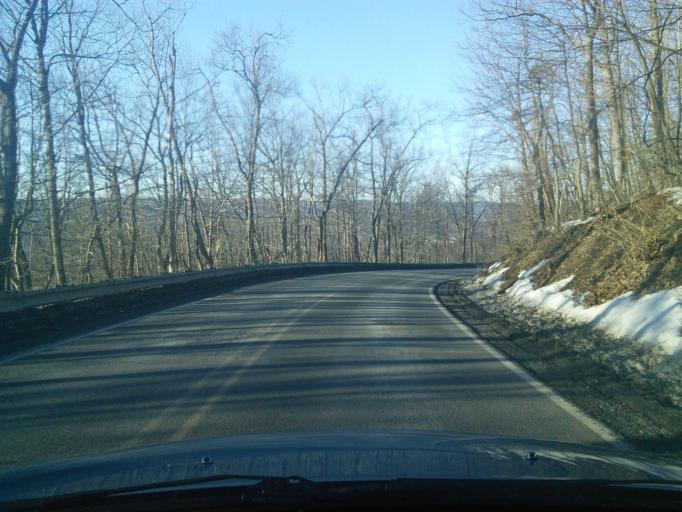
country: US
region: Pennsylvania
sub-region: Centre County
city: Park Forest Village
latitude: 40.8431
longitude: -77.9533
